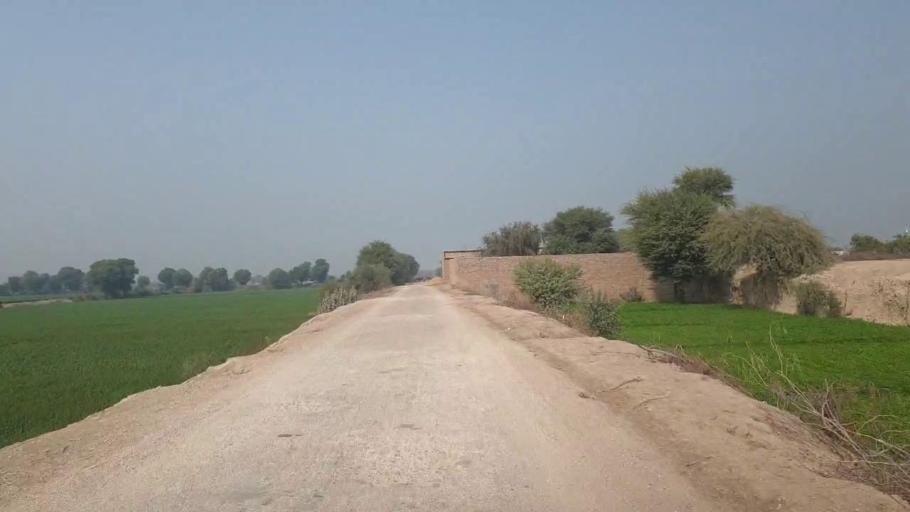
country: PK
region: Sindh
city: Hala
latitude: 25.8188
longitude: 68.4099
